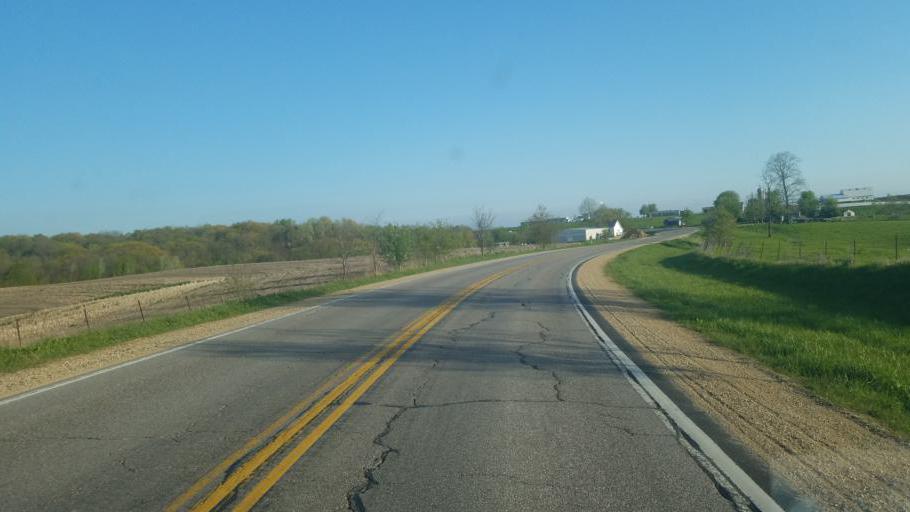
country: US
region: Wisconsin
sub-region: Vernon County
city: Hillsboro
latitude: 43.5942
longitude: -90.4968
